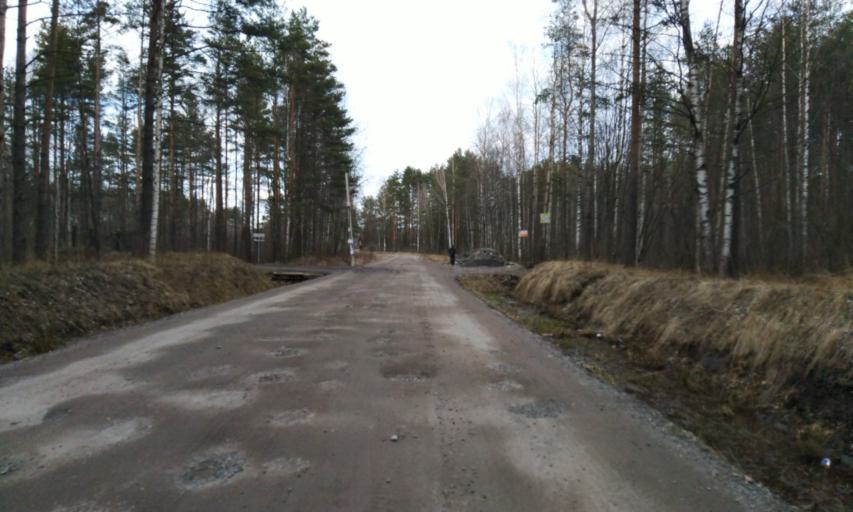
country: RU
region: Leningrad
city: Toksovo
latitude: 60.1180
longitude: 30.4829
